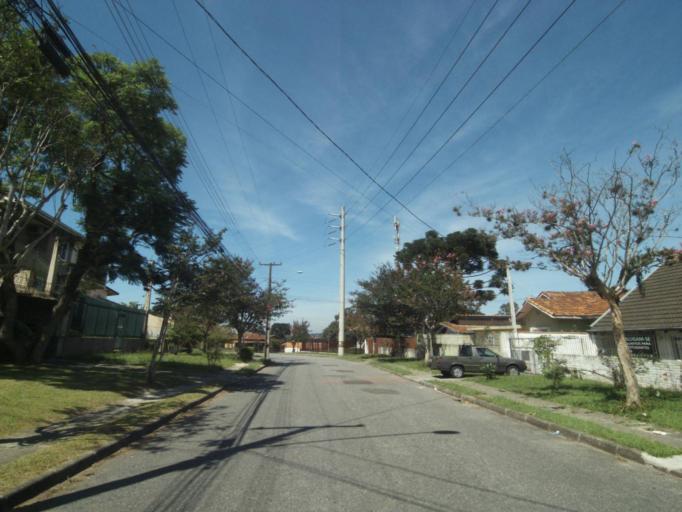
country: BR
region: Parana
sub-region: Curitiba
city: Curitiba
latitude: -25.4593
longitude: -49.2477
